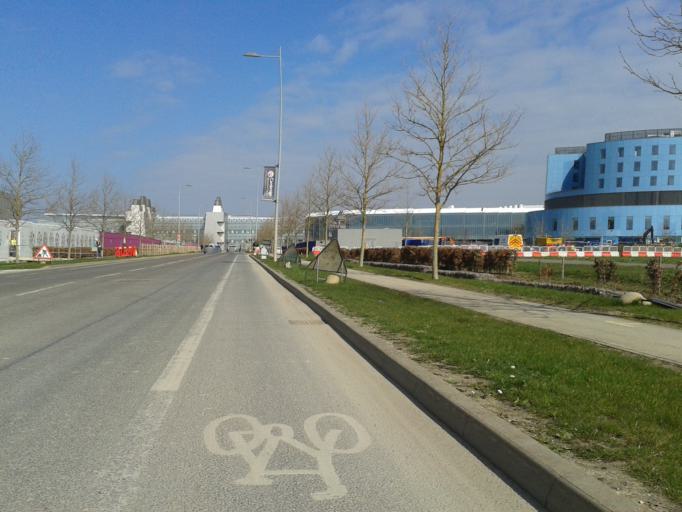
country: GB
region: England
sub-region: Cambridgeshire
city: Cambridge
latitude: 52.1715
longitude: 0.1337
